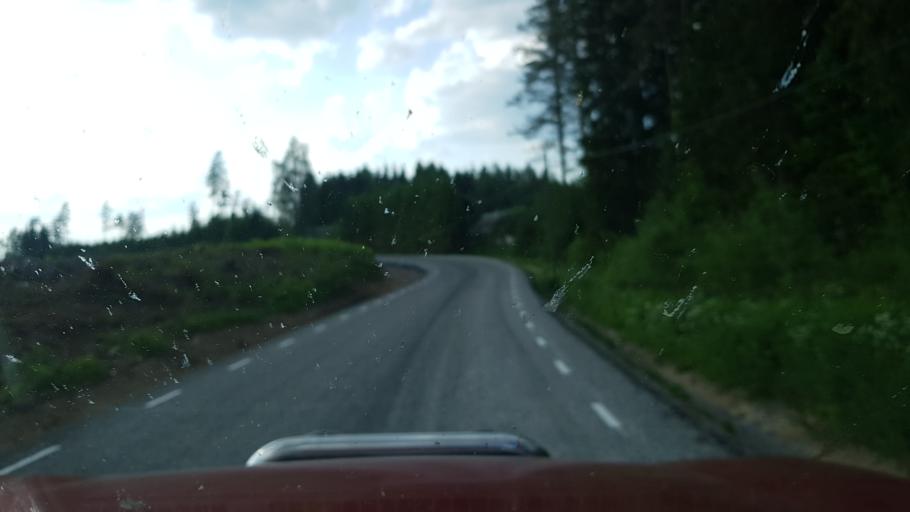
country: EE
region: Tartu
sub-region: UElenurme vald
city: Ulenurme
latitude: 58.1097
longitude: 26.7437
